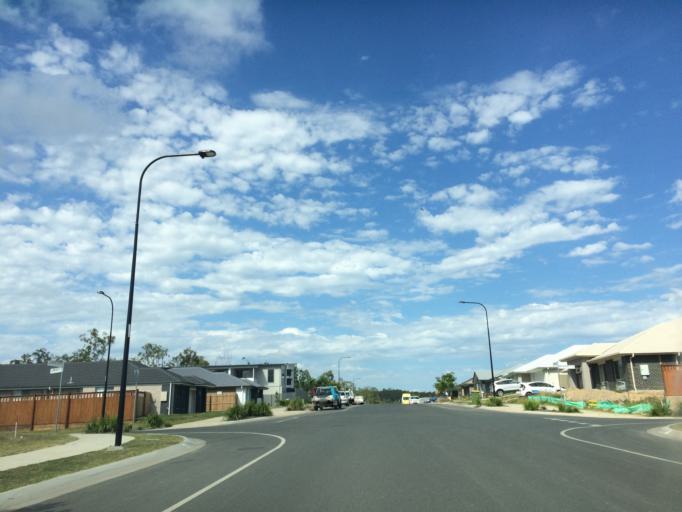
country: AU
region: Queensland
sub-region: Logan
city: North Maclean
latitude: -27.8019
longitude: 152.9436
